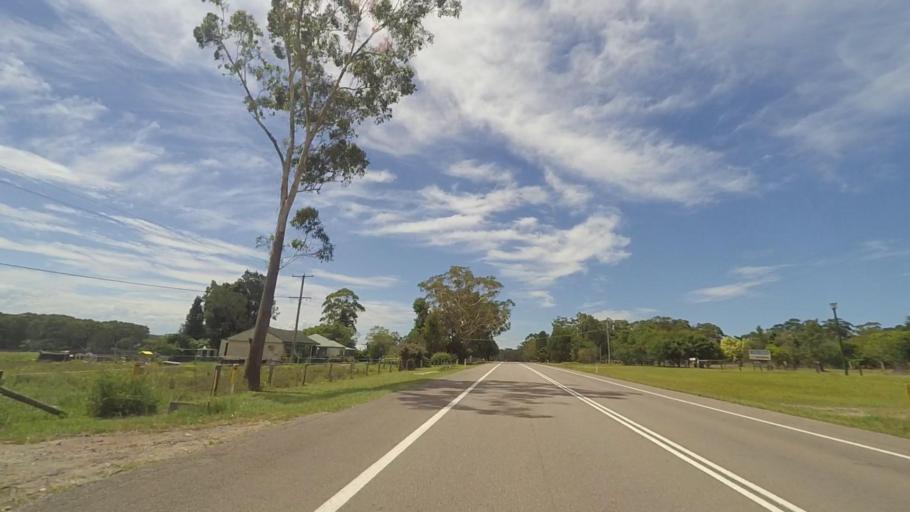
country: AU
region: New South Wales
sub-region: Port Stephens Shire
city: Medowie
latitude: -32.7566
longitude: 151.8670
